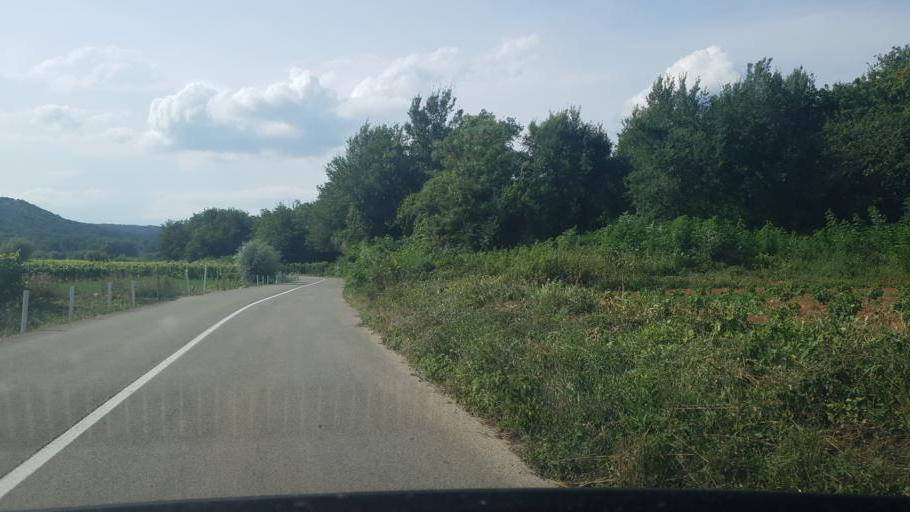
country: HR
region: Primorsko-Goranska
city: Punat
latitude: 45.0844
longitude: 14.6462
